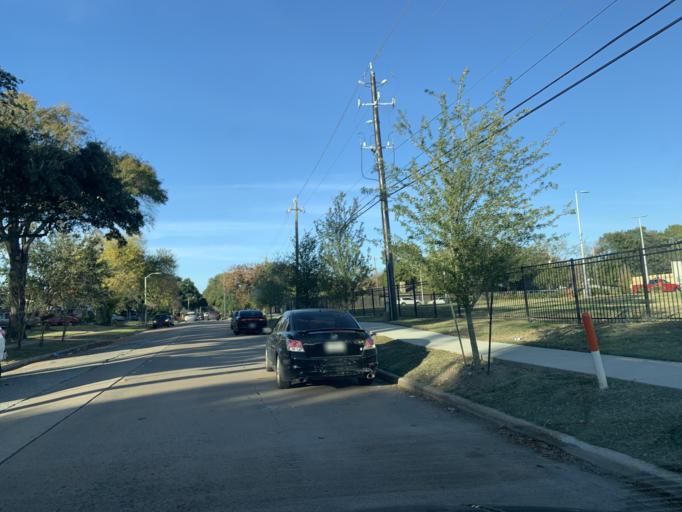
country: US
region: Texas
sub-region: Harris County
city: Bellaire
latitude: 29.6844
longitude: -95.5176
